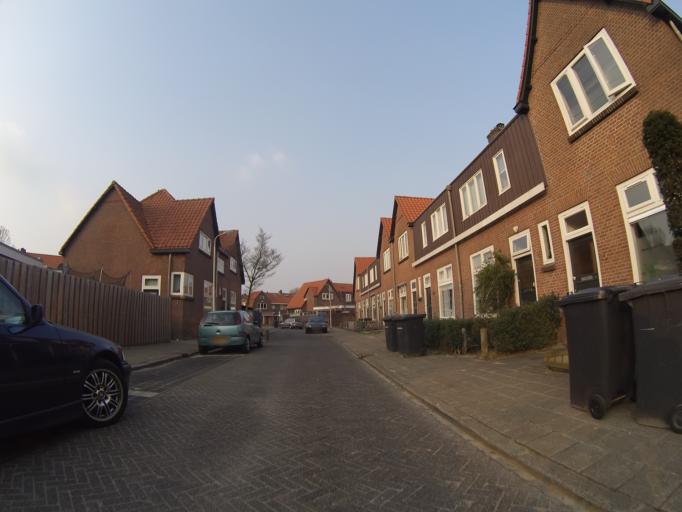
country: NL
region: Utrecht
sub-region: Gemeente Amersfoort
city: Amersfoort
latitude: 52.1610
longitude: 5.3938
